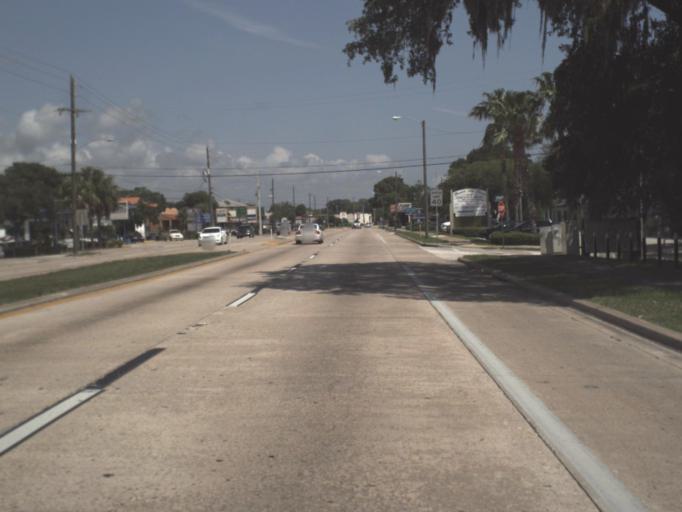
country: US
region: Florida
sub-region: Saint Johns County
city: Saint Augustine
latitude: 29.9123
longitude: -81.3228
